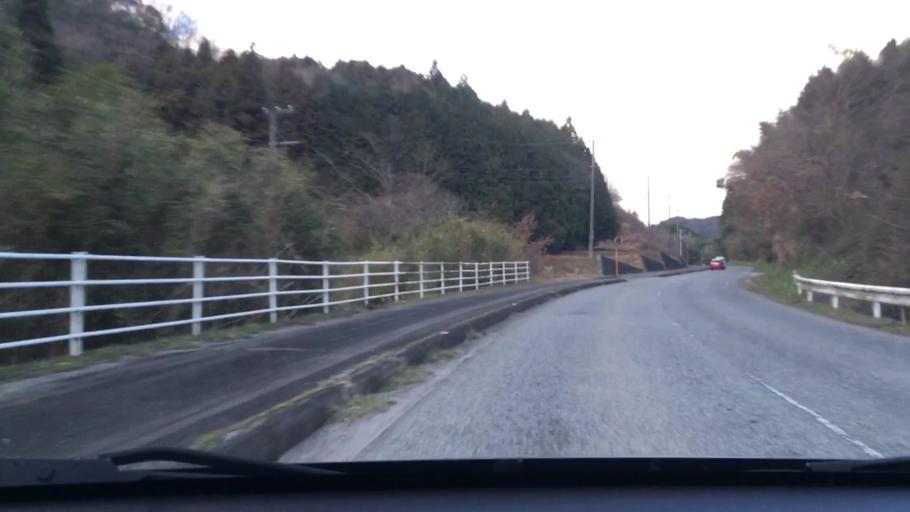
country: JP
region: Oita
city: Bungo-Takada-shi
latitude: 33.4736
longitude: 131.3842
